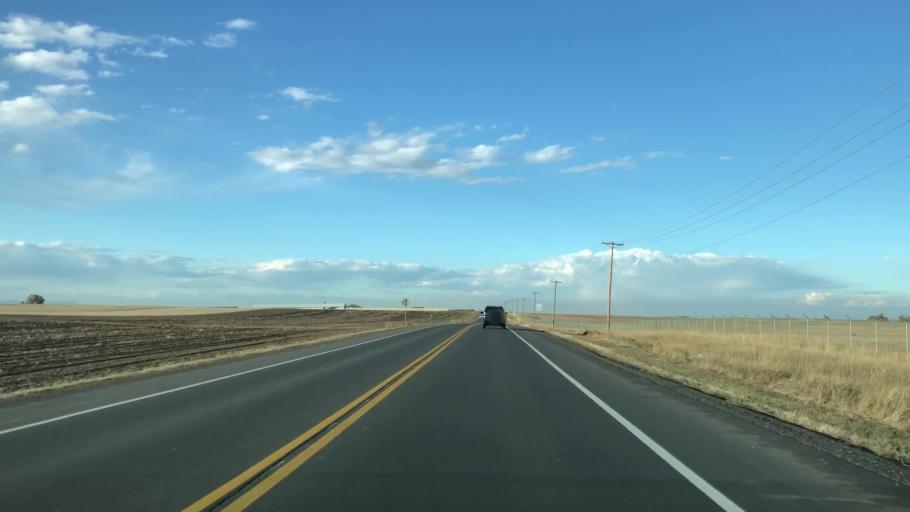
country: US
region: Colorado
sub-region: Larimer County
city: Loveland
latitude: 40.4514
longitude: -105.0205
